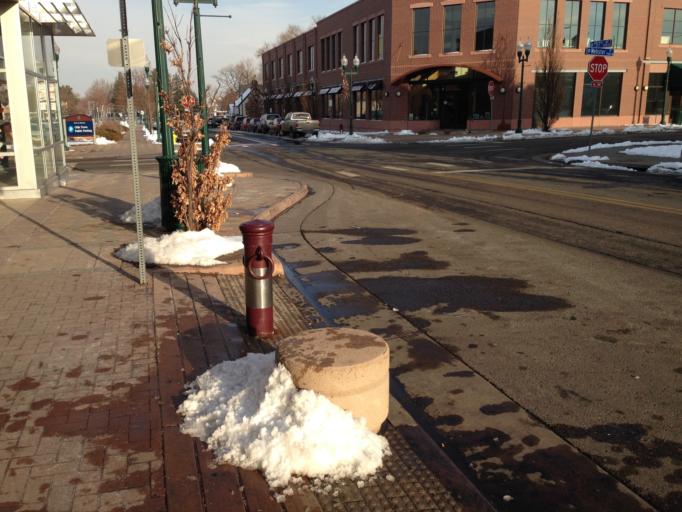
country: US
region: Colorado
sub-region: Jefferson County
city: Arvada
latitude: 39.8002
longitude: -105.0804
